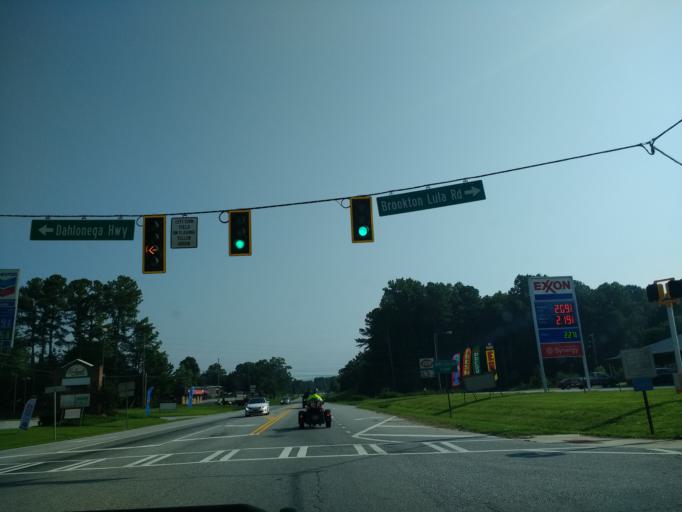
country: US
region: Georgia
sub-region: Hall County
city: Gainesville
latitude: 34.4454
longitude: -83.8057
